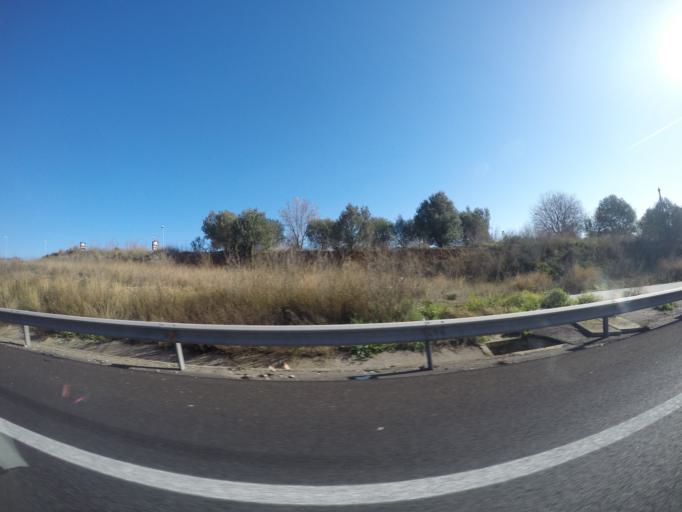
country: ES
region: Catalonia
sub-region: Provincia de Barcelona
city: Esparreguera
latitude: 41.5262
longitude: 1.8811
